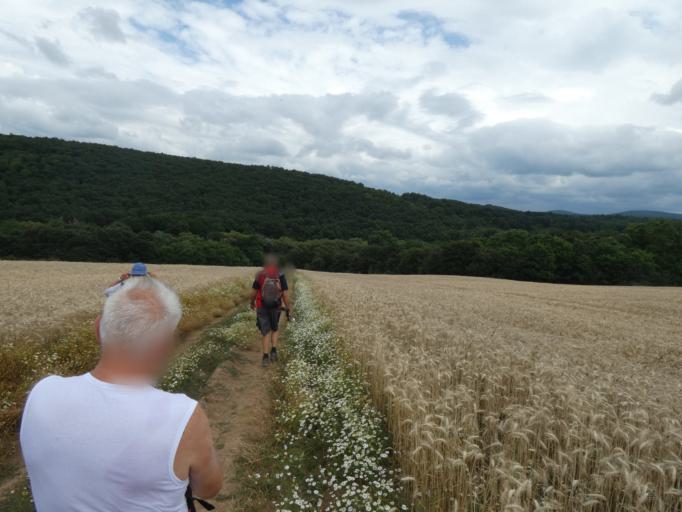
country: HU
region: Pest
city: Szob
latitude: 47.8357
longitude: 18.8922
